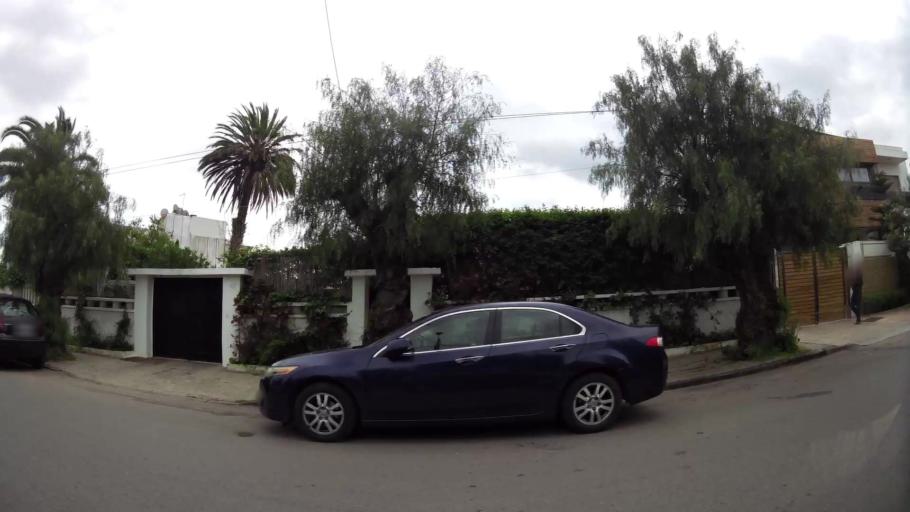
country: MA
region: Grand Casablanca
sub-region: Casablanca
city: Casablanca
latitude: 33.5563
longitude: -7.6371
